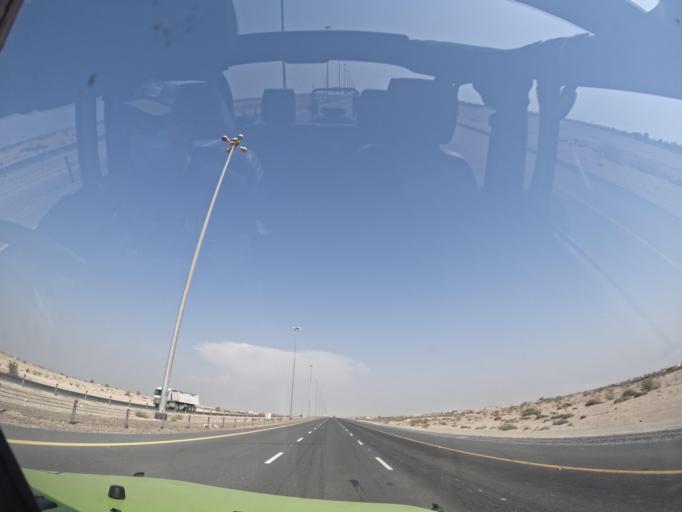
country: AE
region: Dubai
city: Dubai
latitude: 24.6763
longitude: 54.8371
